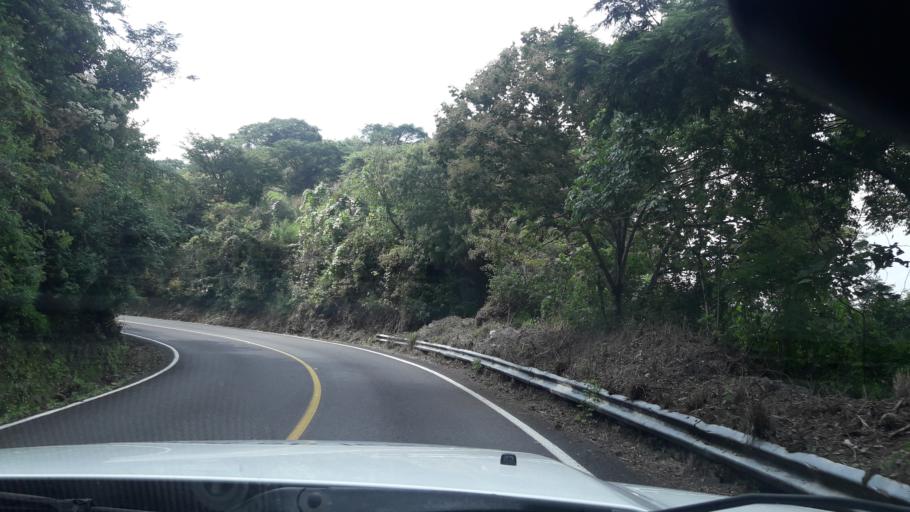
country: MX
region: Colima
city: Suchitlan
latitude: 19.4384
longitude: -103.7131
